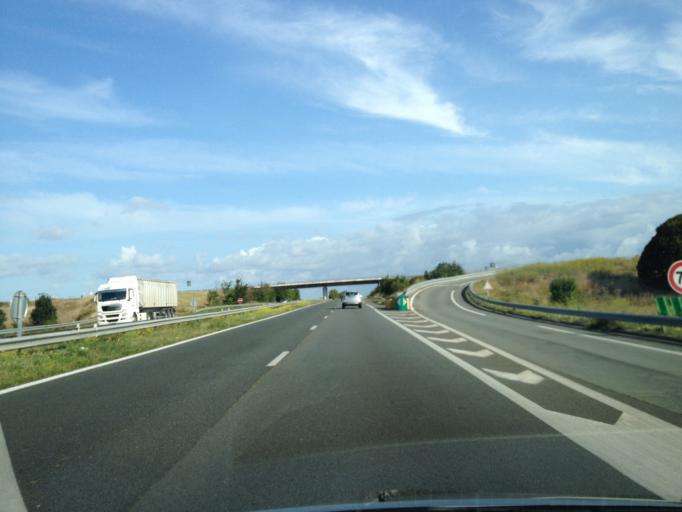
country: FR
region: Poitou-Charentes
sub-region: Departement de la Charente-Maritime
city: Chatelaillon-Plage
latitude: 46.0615
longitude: -1.0608
